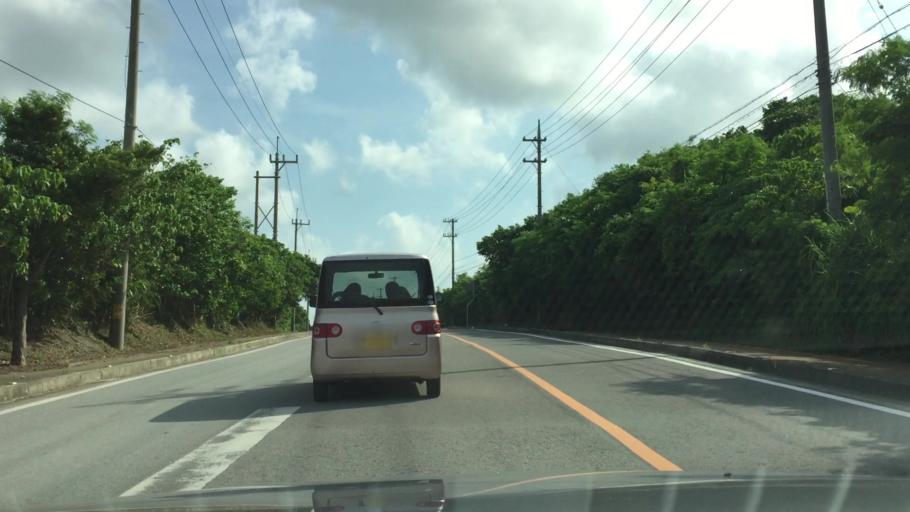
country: JP
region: Okinawa
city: Ishigaki
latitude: 24.4285
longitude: 124.2465
